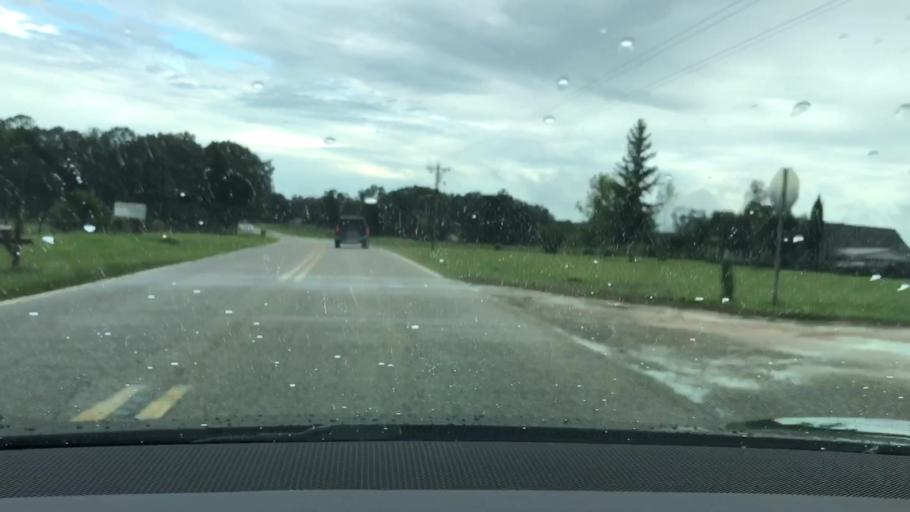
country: US
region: Alabama
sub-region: Geneva County
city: Samson
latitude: 31.1202
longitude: -86.1238
